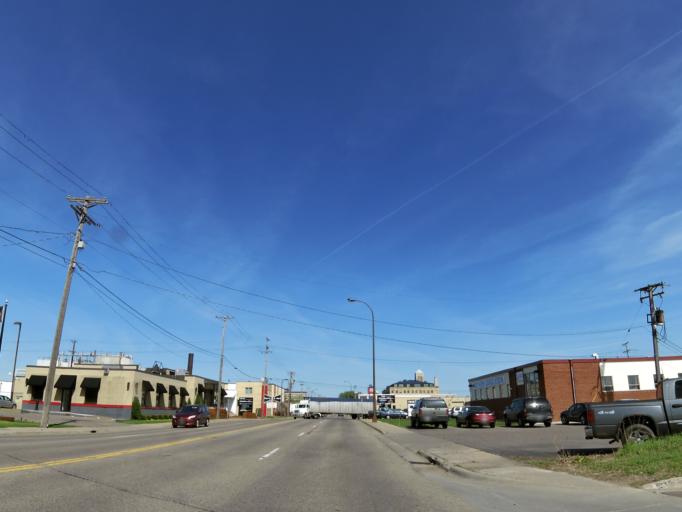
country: US
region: Minnesota
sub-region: Hennepin County
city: Saint Anthony
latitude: 44.9986
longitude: -93.2335
